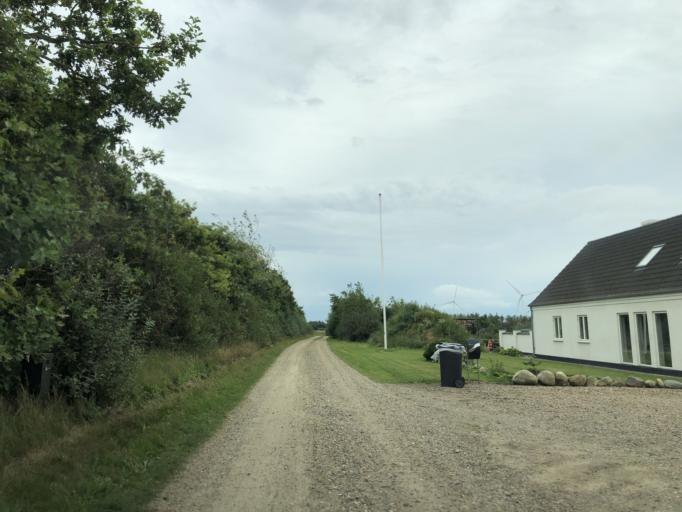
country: DK
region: Central Jutland
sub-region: Ringkobing-Skjern Kommune
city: Ringkobing
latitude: 56.1308
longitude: 8.2514
